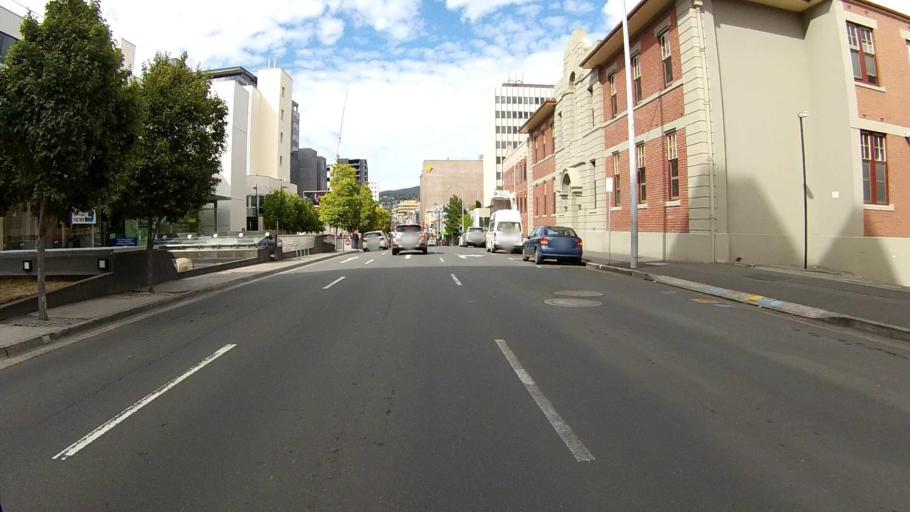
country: AU
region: Tasmania
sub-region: Hobart
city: Hobart
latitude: -42.8795
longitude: 147.3292
